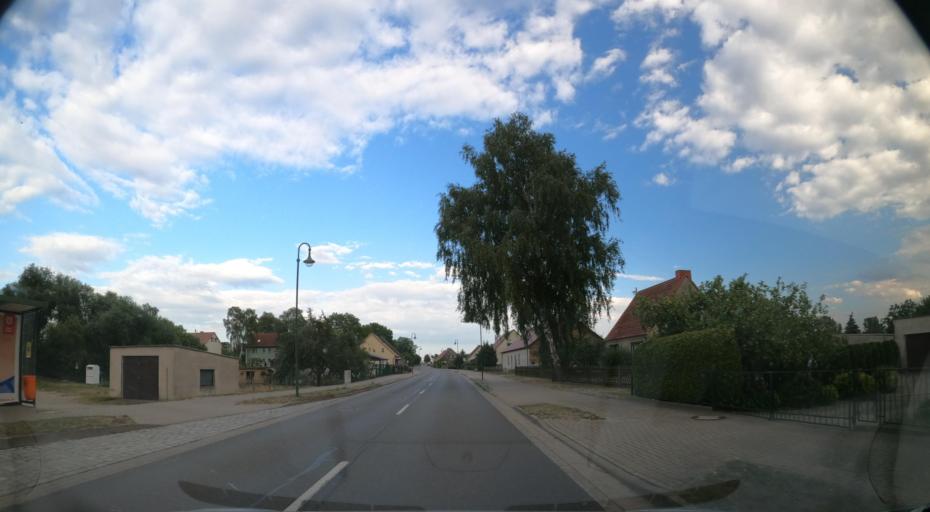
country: DE
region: Brandenburg
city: Brussow
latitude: 53.4718
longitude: 14.1350
